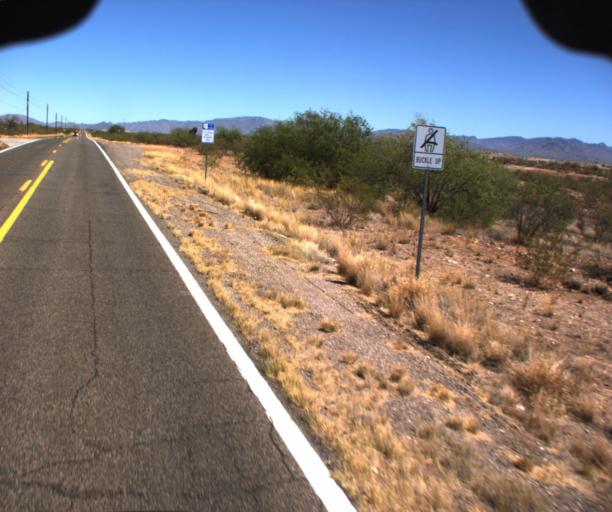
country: US
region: Arizona
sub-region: Maricopa County
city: Wickenburg
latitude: 34.0360
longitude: -112.8126
